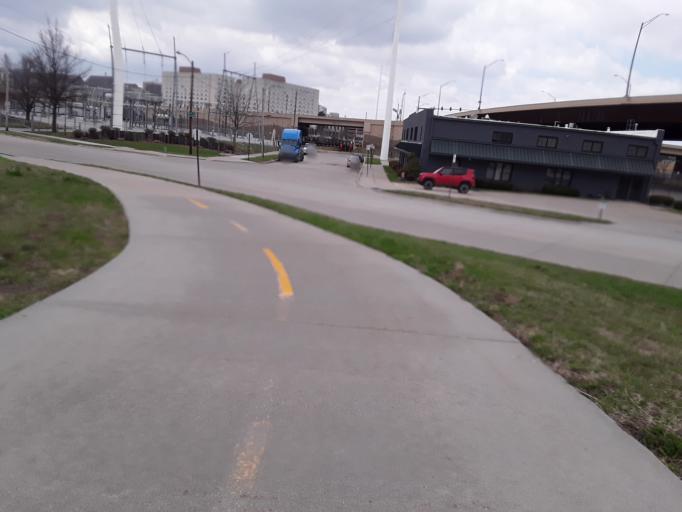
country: US
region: Nebraska
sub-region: Lancaster County
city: Lincoln
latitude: 40.8278
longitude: -96.6962
